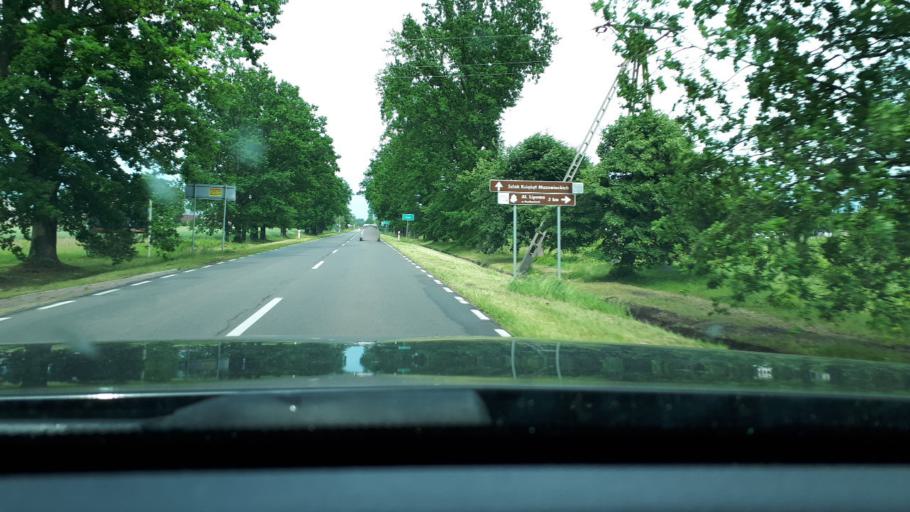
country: PL
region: Masovian Voivodeship
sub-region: Powiat sochaczewski
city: Paprotnia
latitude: 52.2684
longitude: 20.3925
